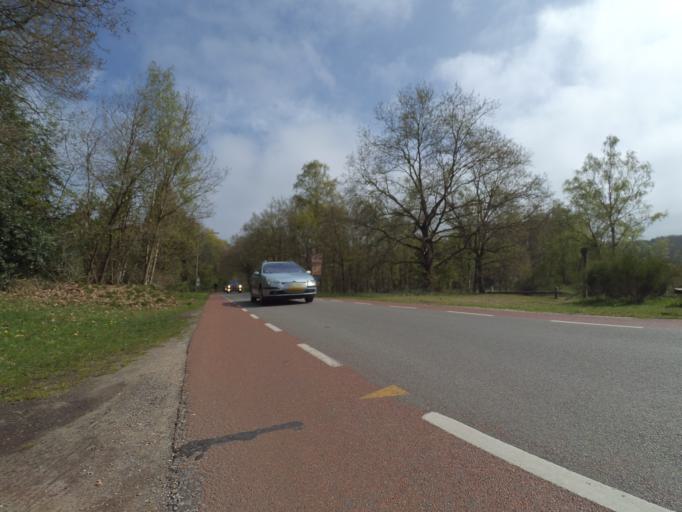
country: NL
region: Gelderland
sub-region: Gemeente Nunspeet
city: Nunspeet
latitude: 52.3259
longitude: 5.8241
